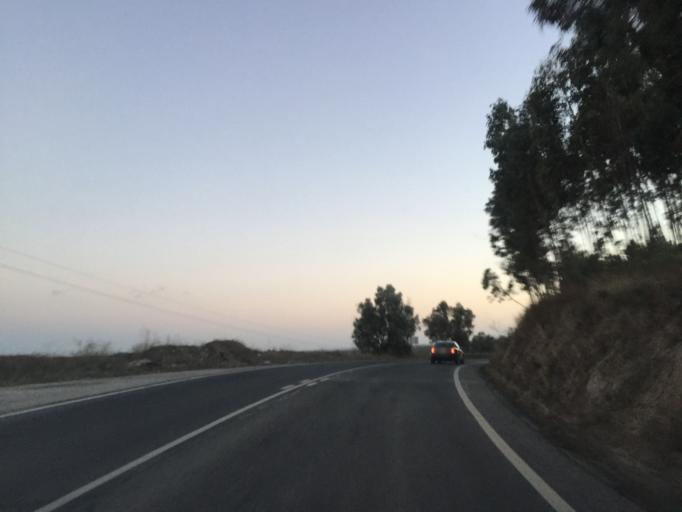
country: PT
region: Lisbon
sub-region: Alenquer
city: Alenquer
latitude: 39.1274
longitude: -8.9915
